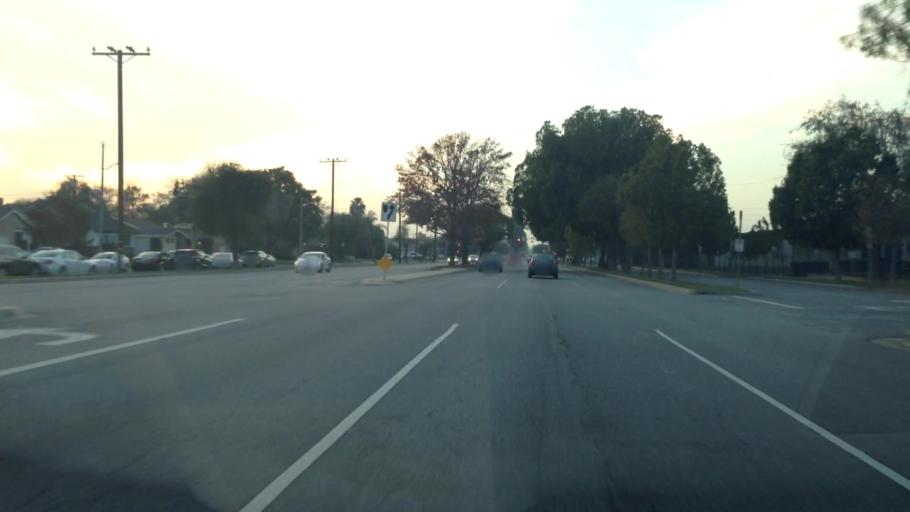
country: US
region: California
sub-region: Orange County
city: Rossmoor
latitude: 33.8033
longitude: -118.1051
